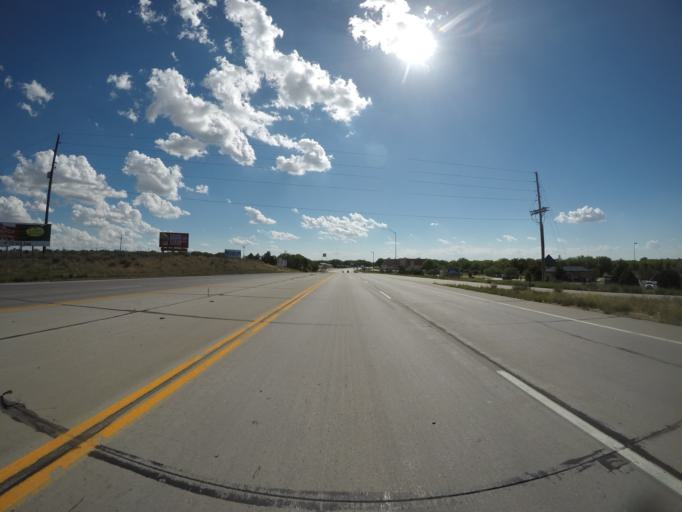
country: US
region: Colorado
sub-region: Logan County
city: Sterling
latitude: 40.6198
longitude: -103.1780
